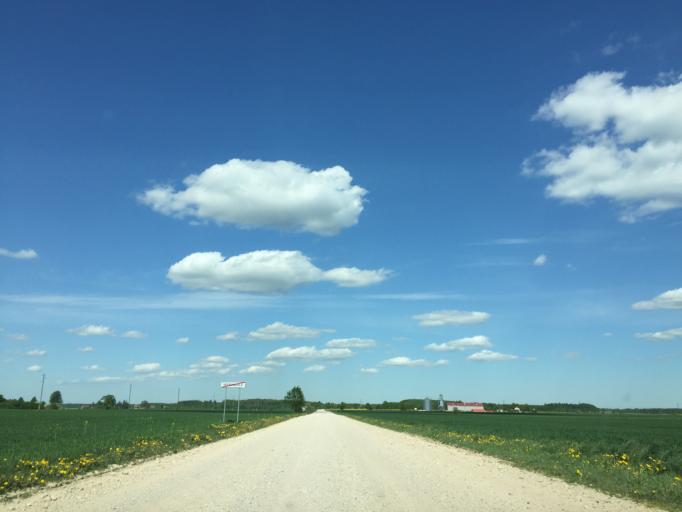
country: LV
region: Rundales
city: Pilsrundale
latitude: 56.3591
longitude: 24.0224
